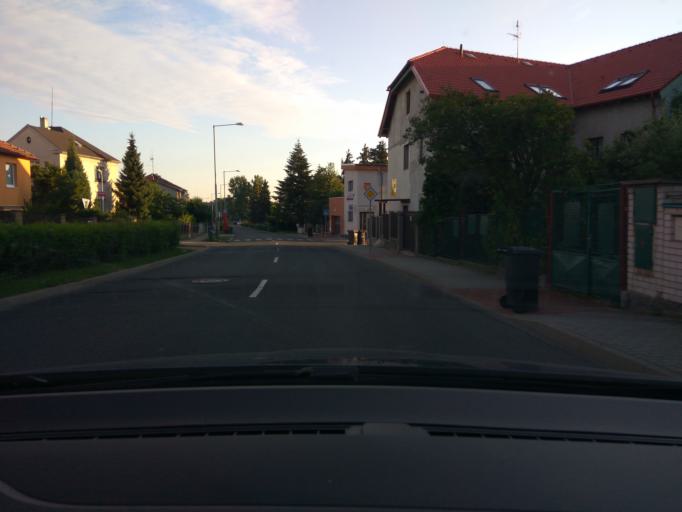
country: CZ
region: Praha
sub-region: Praha 18
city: Letnany
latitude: 50.1537
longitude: 14.5287
